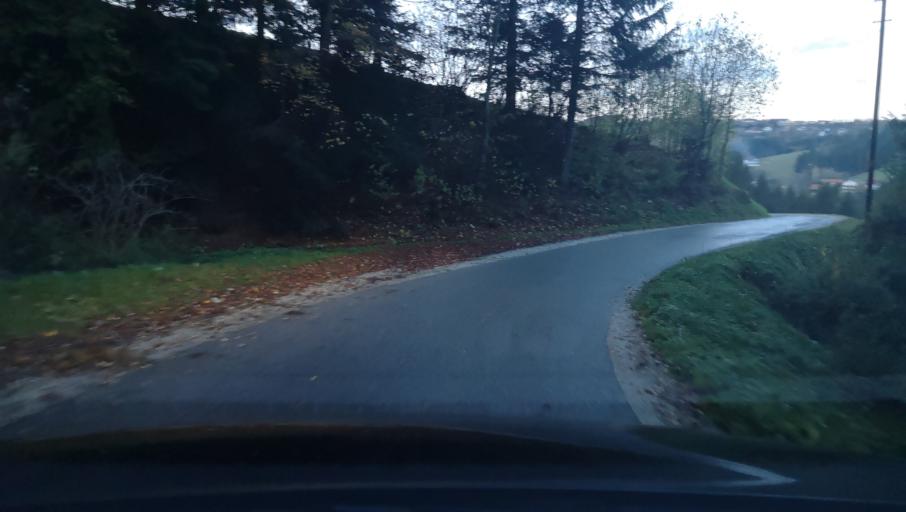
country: AT
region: Styria
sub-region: Politischer Bezirk Weiz
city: Birkfeld
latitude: 47.3359
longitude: 15.6842
